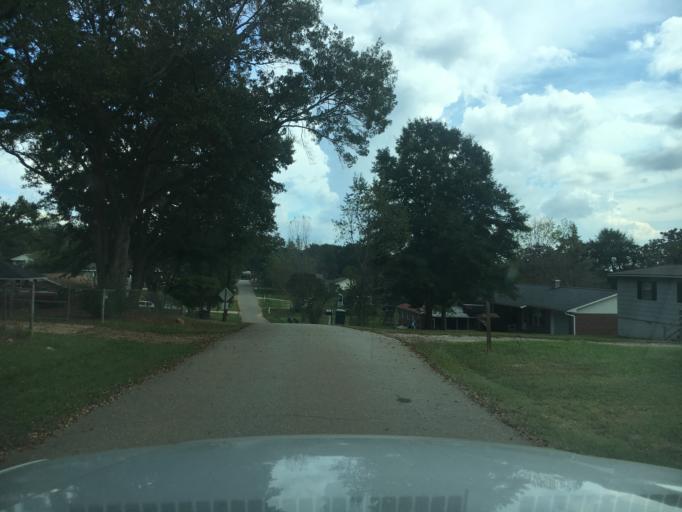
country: US
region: South Carolina
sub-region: Spartanburg County
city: Duncan
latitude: 34.9503
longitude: -82.1679
